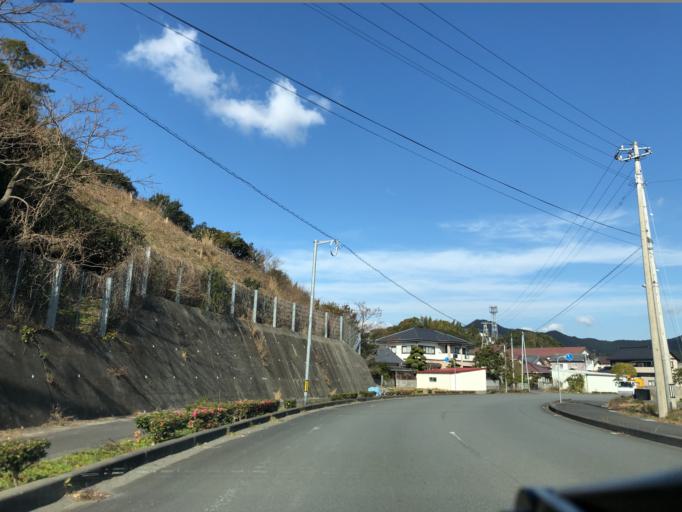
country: JP
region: Kochi
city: Sukumo
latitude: 32.9216
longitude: 132.7017
